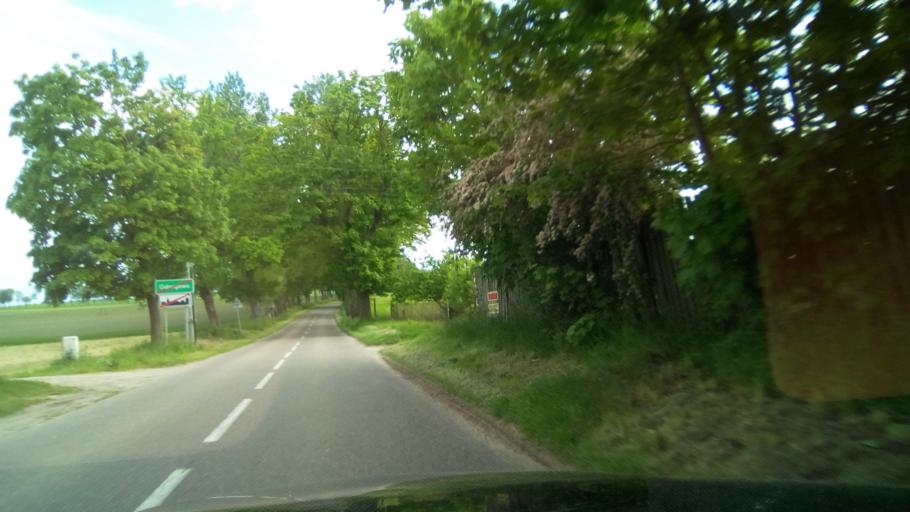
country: PL
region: Pomeranian Voivodeship
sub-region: Powiat pucki
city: Krokowa
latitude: 54.7930
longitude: 18.1169
